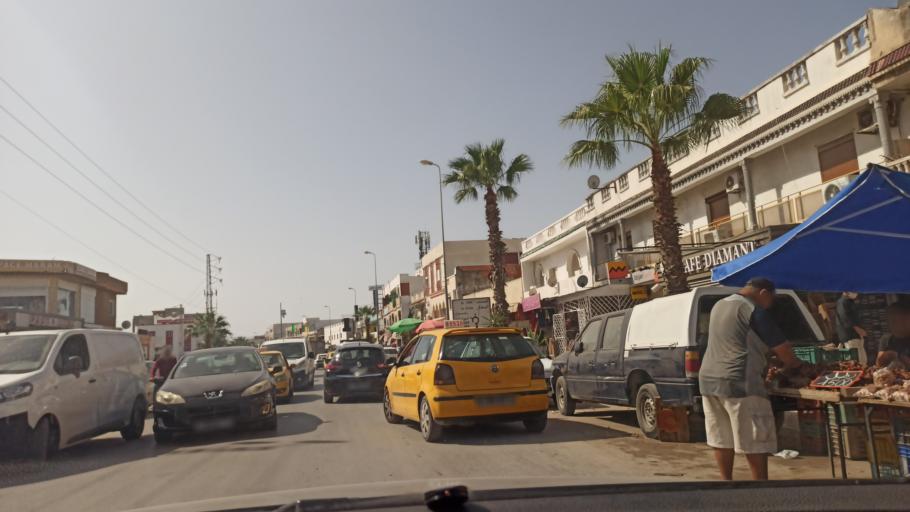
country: TN
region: Manouba
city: Manouba
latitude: 36.7716
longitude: 10.1136
